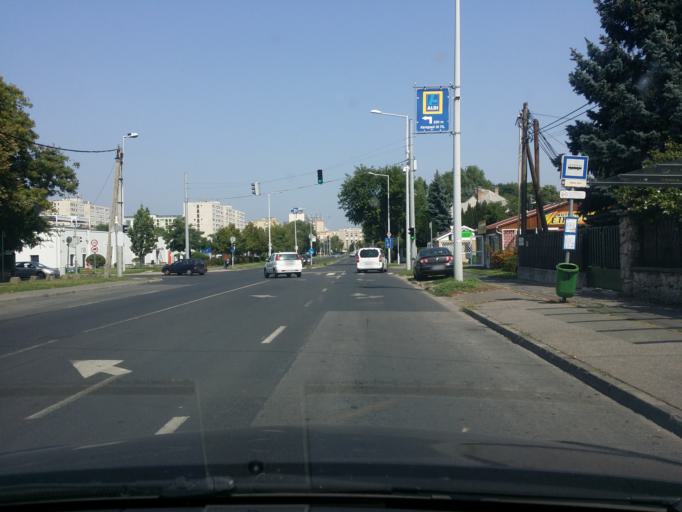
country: HU
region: Budapest
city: Budapest XVI. keruelet
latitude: 47.5024
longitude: 19.1533
